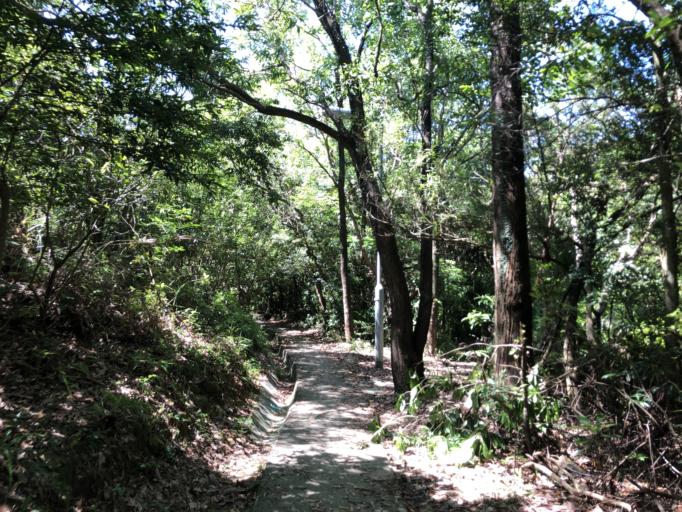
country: HK
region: Tuen Mun
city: Tuen Mun
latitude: 22.2786
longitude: 113.9885
